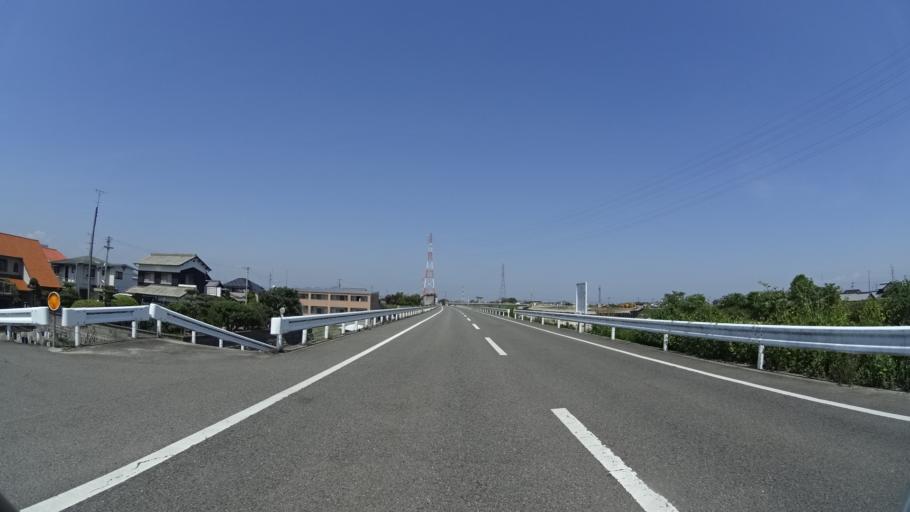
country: JP
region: Ehime
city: Hojo
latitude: 34.0359
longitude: 132.9733
